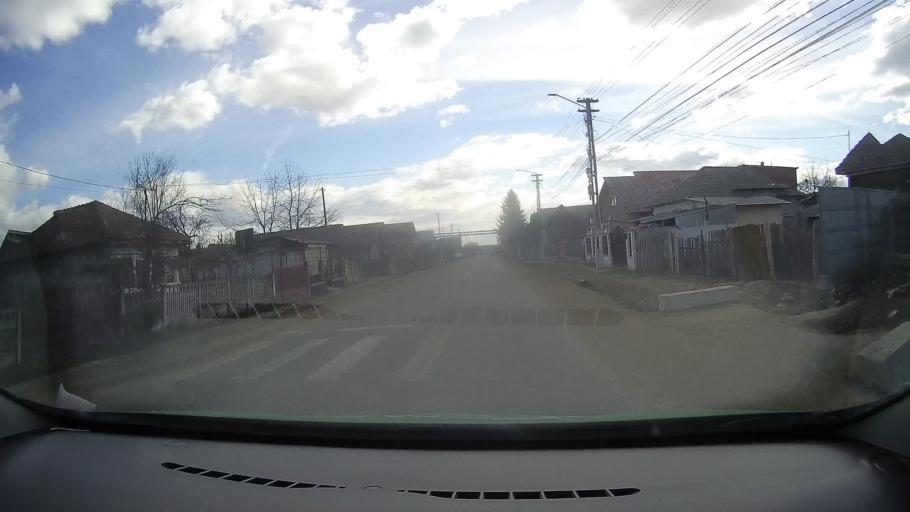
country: RO
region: Dambovita
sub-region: Comuna Doicesti
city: Doicesti
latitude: 44.9824
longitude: 25.3884
